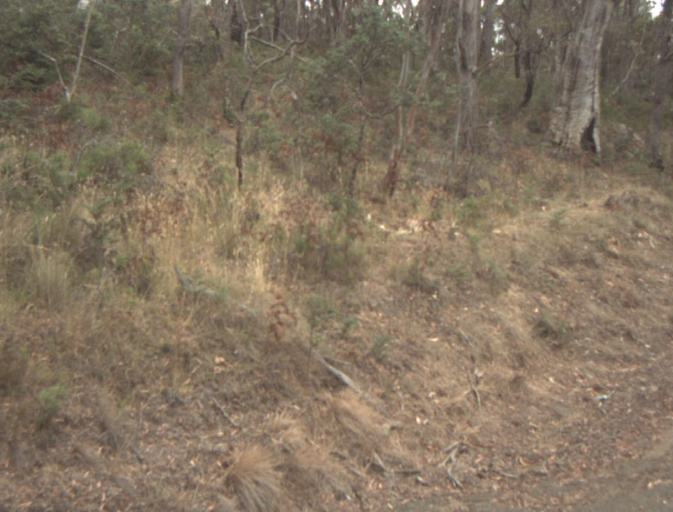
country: AU
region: Tasmania
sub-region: Northern Midlands
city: Evandale
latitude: -41.4819
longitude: 147.5360
